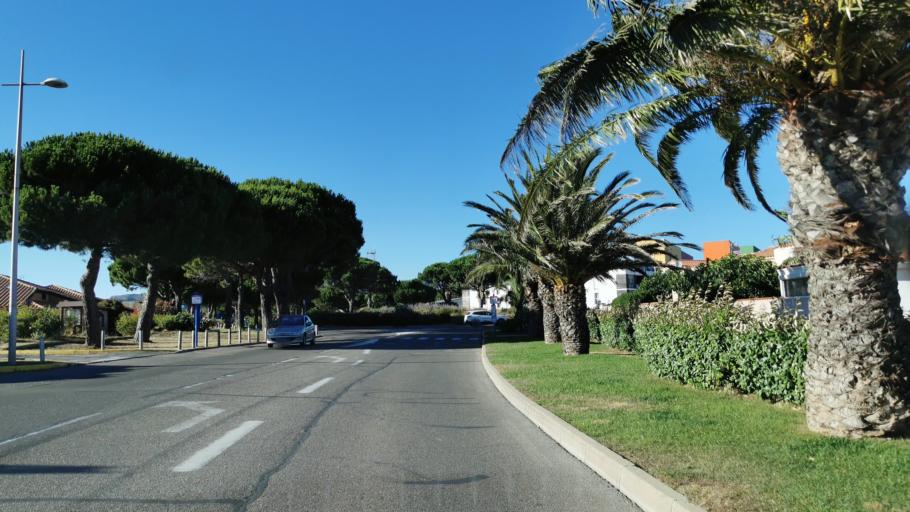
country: FR
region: Languedoc-Roussillon
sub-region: Departement de l'Aude
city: Gruissan
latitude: 43.1131
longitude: 3.1038
